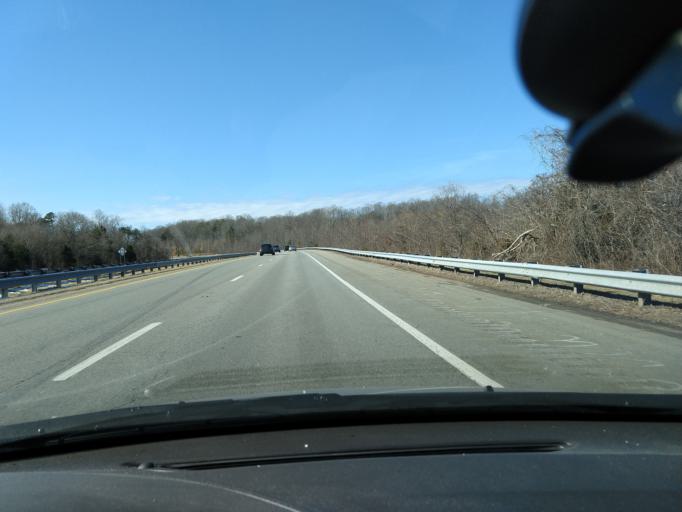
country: US
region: North Carolina
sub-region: Guilford County
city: Summerfield
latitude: 36.1167
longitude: -79.8927
